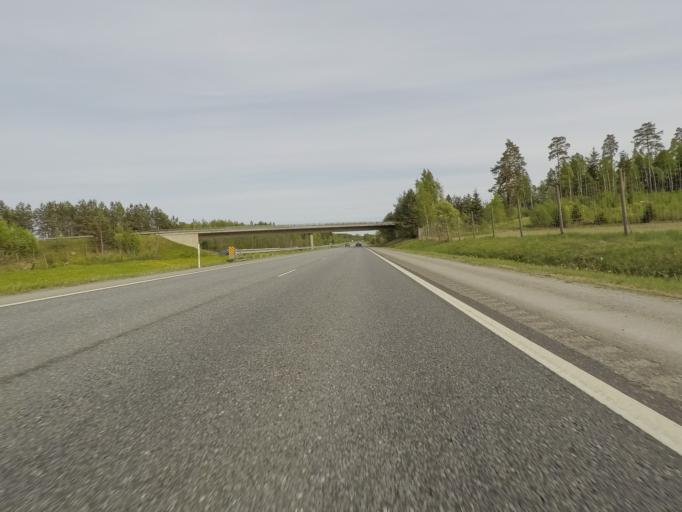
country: FI
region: Haeme
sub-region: Haemeenlinna
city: Tervakoski
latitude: 60.8445
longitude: 24.6256
